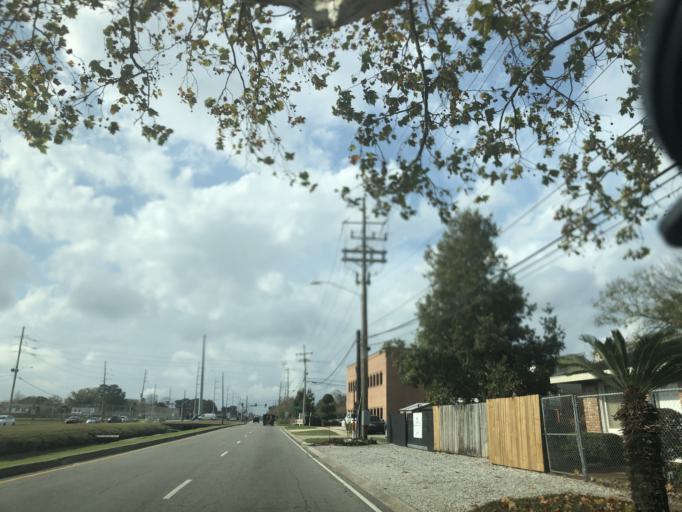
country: US
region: Louisiana
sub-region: Jefferson Parish
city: Metairie
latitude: 29.9925
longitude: -90.1576
